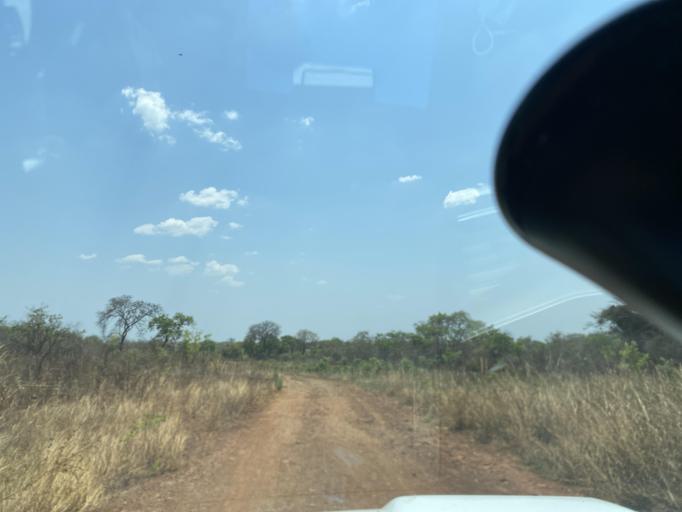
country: ZM
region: Lusaka
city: Lusaka
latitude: -15.5048
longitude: 28.0122
